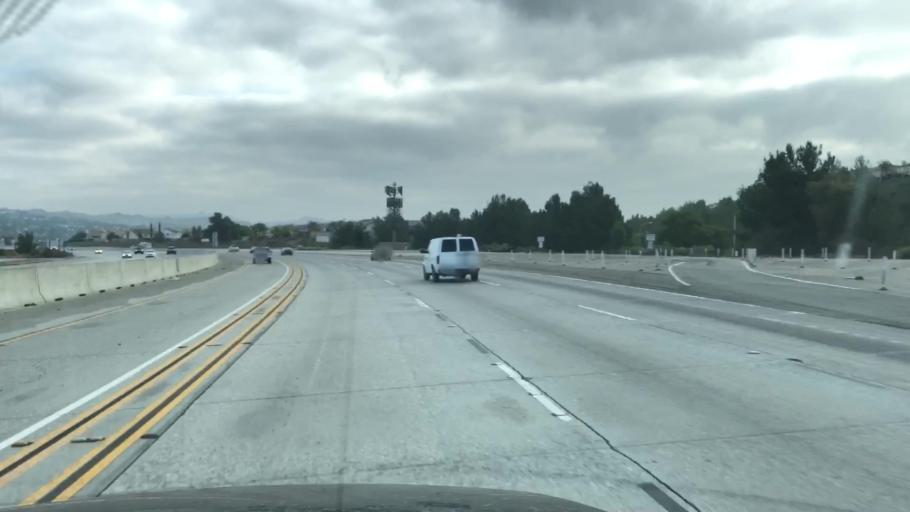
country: US
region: California
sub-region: Los Angeles County
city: Santa Clarita
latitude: 34.4052
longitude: -118.4500
